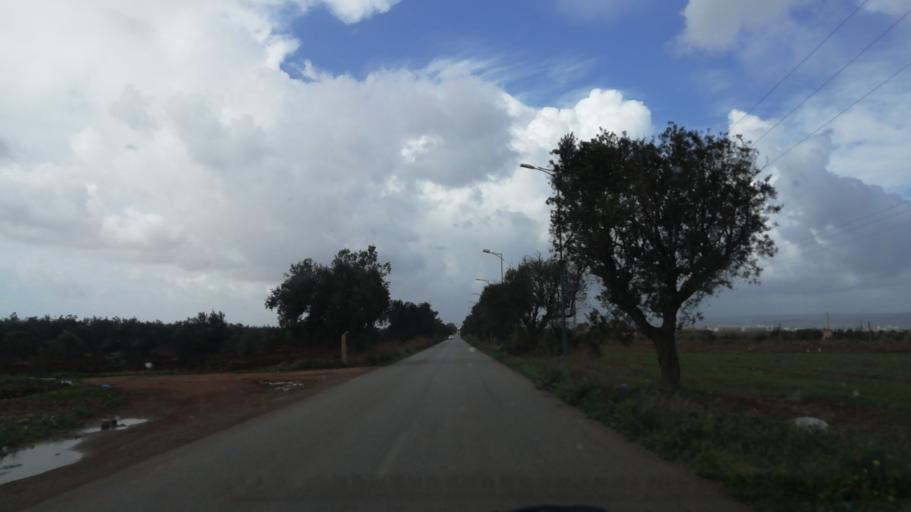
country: DZ
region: Oran
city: Sidi ech Chahmi
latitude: 35.6226
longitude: -0.5551
